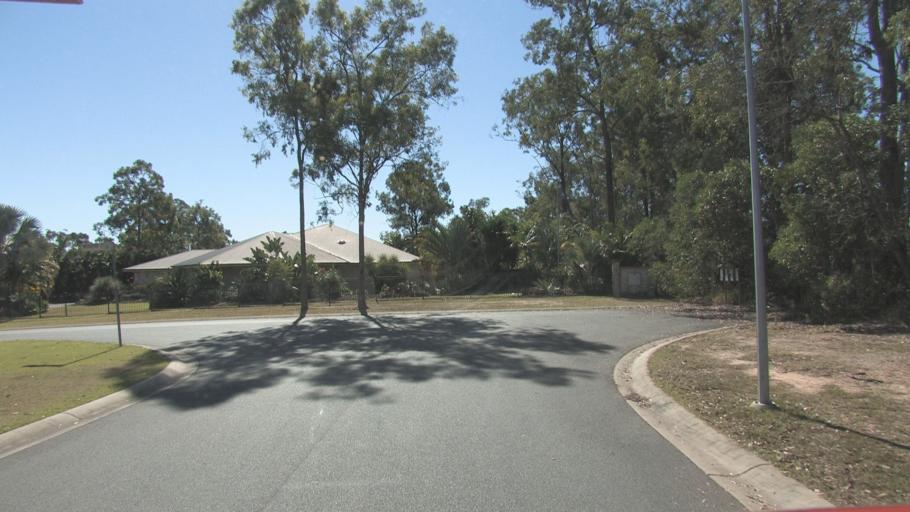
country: AU
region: Queensland
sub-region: Logan
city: Park Ridge South
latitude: -27.7144
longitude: 153.0461
